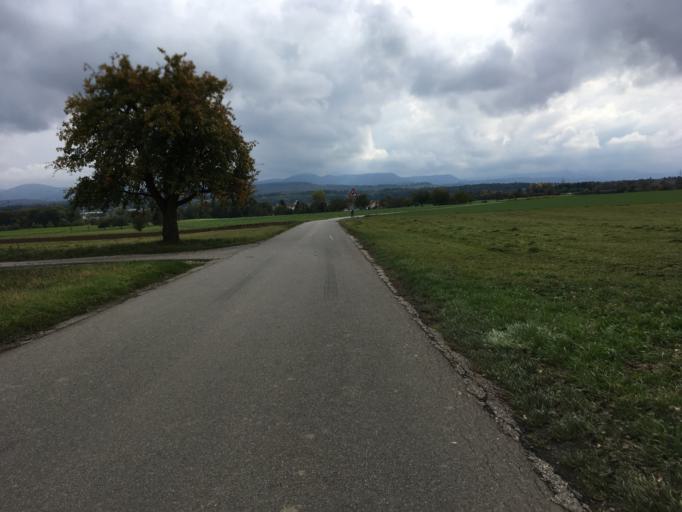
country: DE
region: Baden-Wuerttemberg
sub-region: Tuebingen Region
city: Kusterdingen
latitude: 48.5104
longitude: 9.1244
